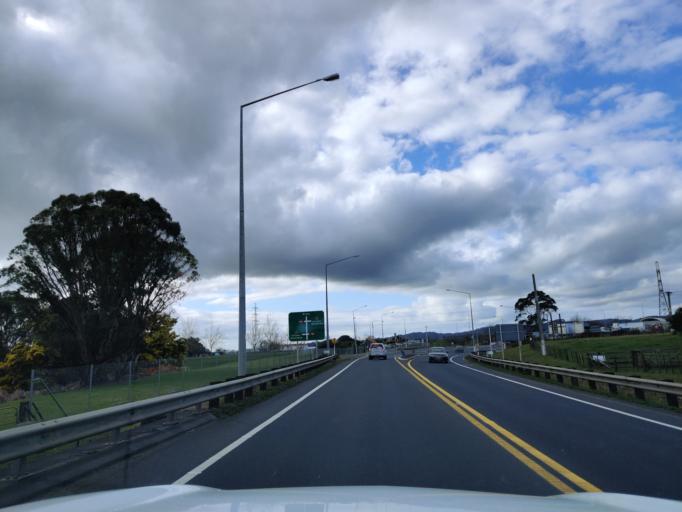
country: NZ
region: Auckland
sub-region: Auckland
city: Papakura
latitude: -37.1096
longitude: 174.9430
